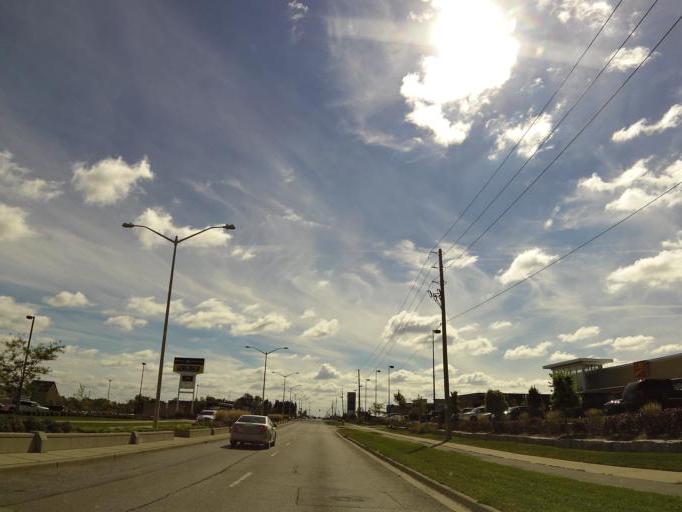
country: CA
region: Ontario
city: London
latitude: 42.9353
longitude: -81.2806
